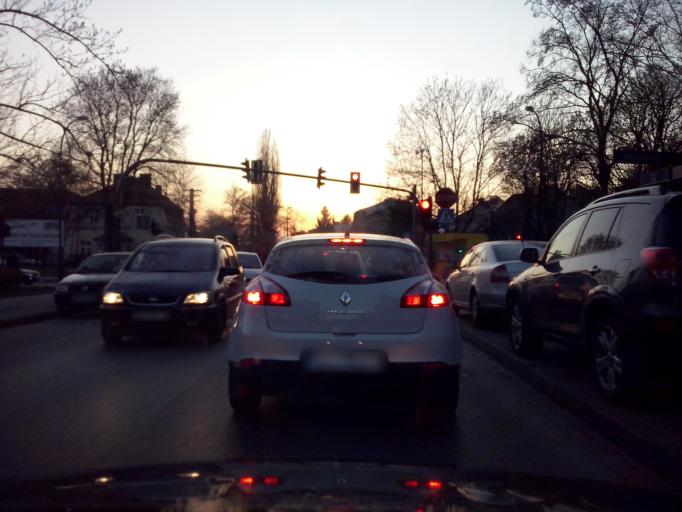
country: PL
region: Lesser Poland Voivodeship
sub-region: Krakow
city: Krakow
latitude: 50.0723
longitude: 19.9056
